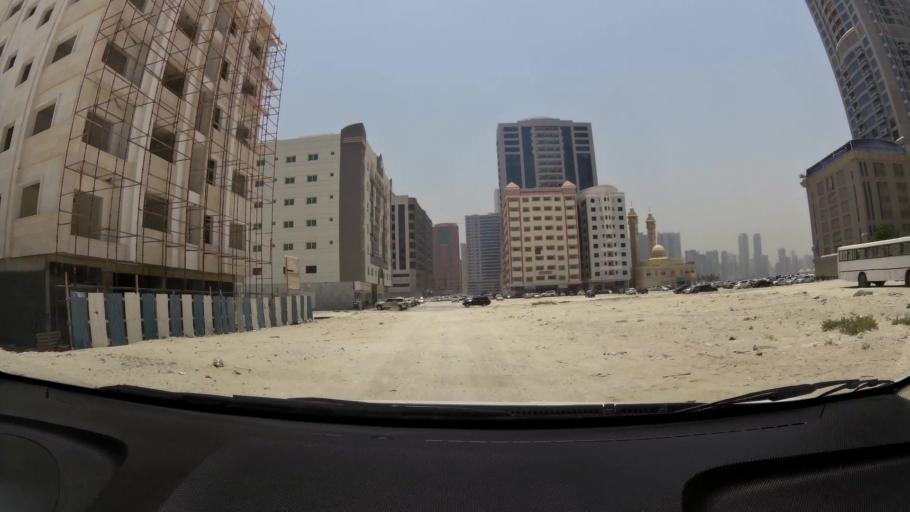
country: AE
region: Ash Shariqah
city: Sharjah
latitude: 25.3306
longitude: 55.3659
